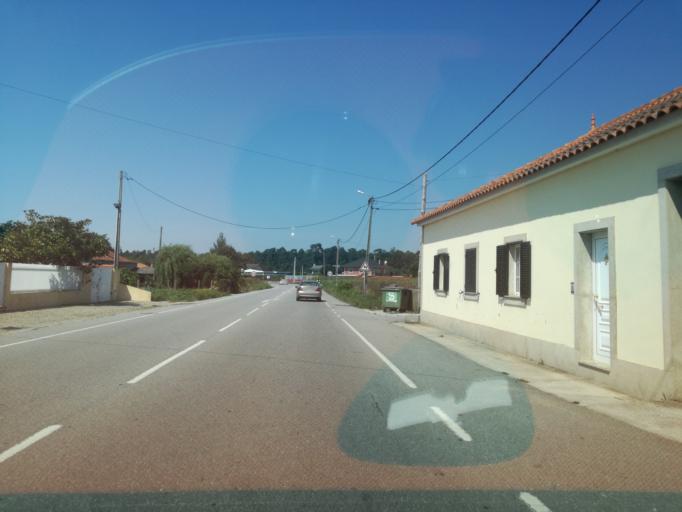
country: PT
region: Braga
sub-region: Esposende
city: Apulia
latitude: 41.4778
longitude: -8.7463
